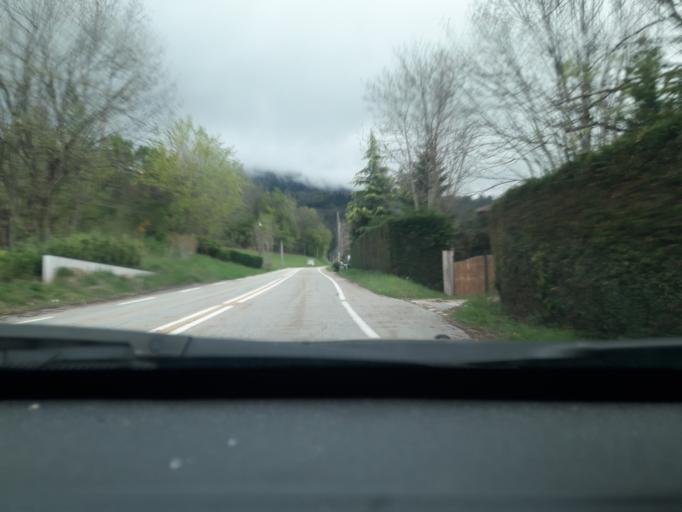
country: FR
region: Rhone-Alpes
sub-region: Departement de l'Isere
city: Vaulnaveys-le-Haut
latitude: 45.1171
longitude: 5.8287
